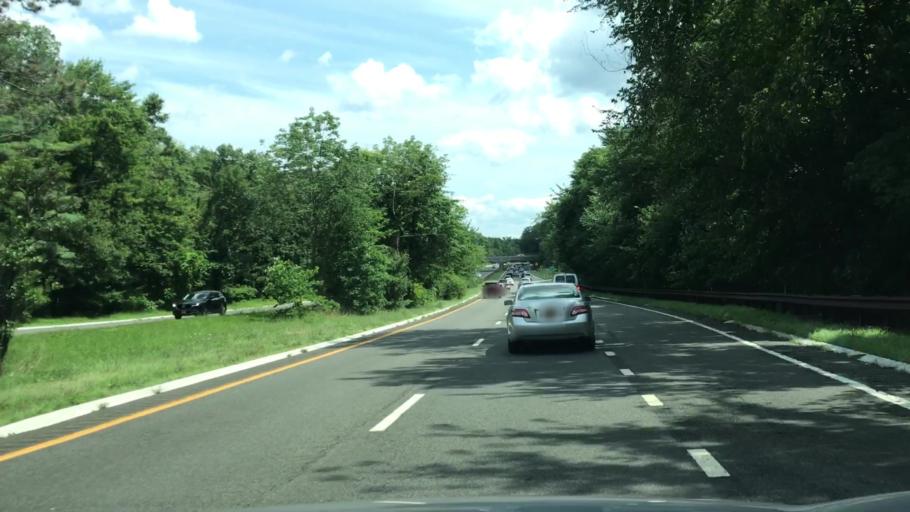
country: US
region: New York
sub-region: Rockland County
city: Bardonia
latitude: 41.1239
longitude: -74.0114
